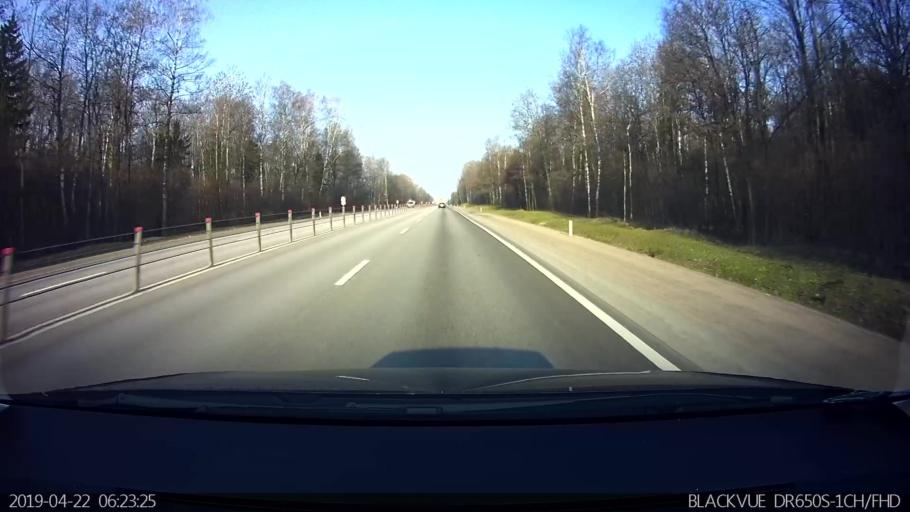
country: RU
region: Moskovskaya
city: Uvarovka
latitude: 55.4651
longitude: 35.8115
